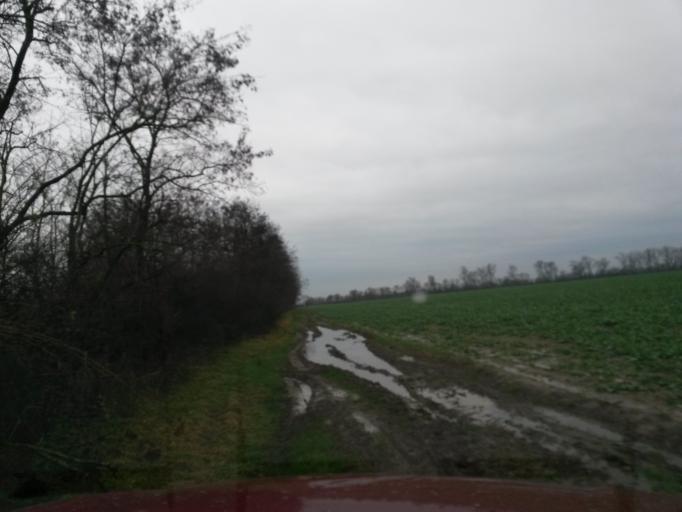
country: SK
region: Kosicky
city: Sobrance
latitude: 48.6416
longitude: 22.0876
